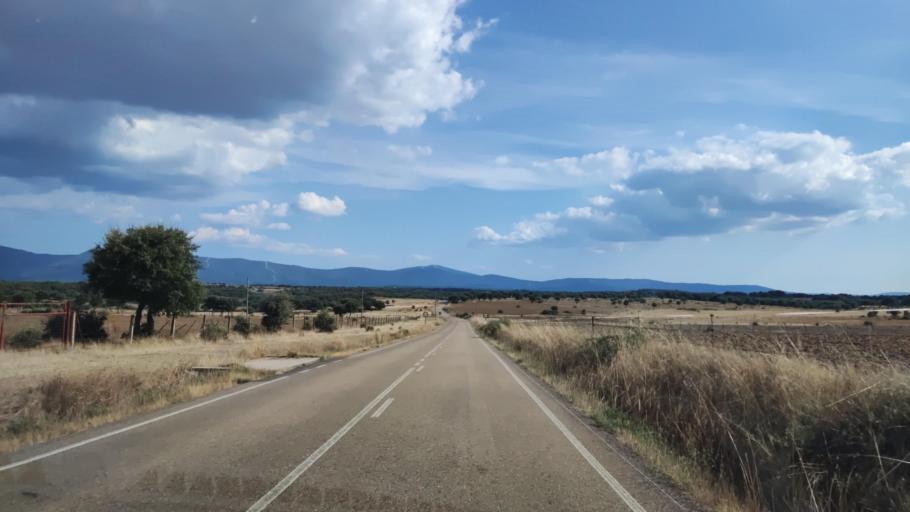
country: ES
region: Castille and Leon
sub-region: Provincia de Salamanca
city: Martiago
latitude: 40.4836
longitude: -6.4934
